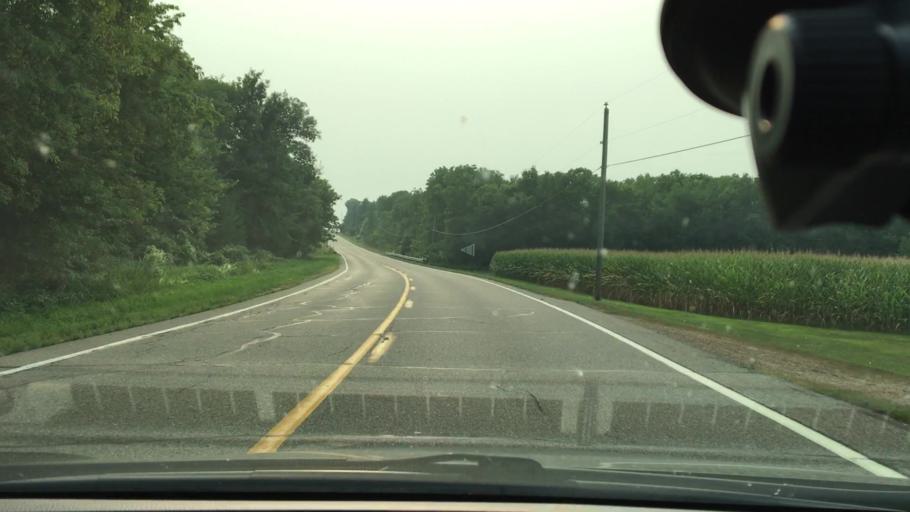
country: US
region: Minnesota
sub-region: Anoka County
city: Ramsey
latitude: 45.2240
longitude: -93.4713
